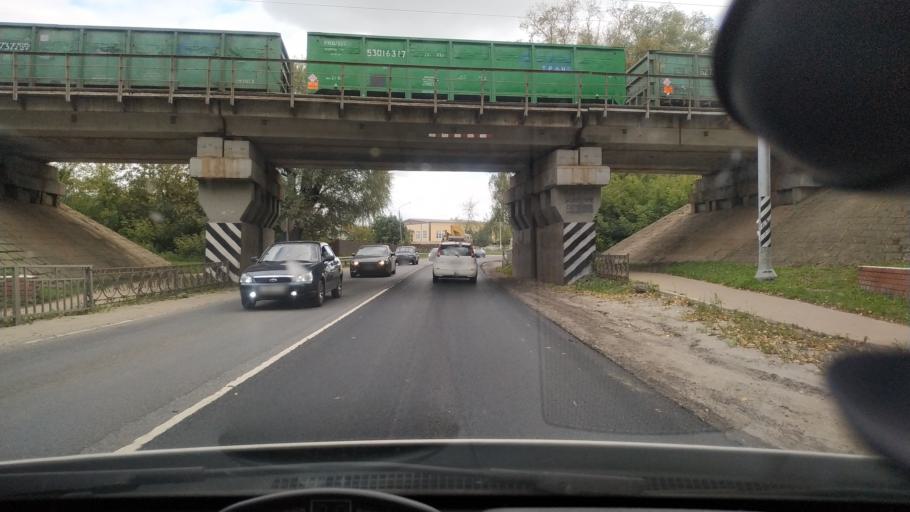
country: RU
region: Moskovskaya
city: Likino-Dulevo
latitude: 55.7298
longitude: 38.9561
